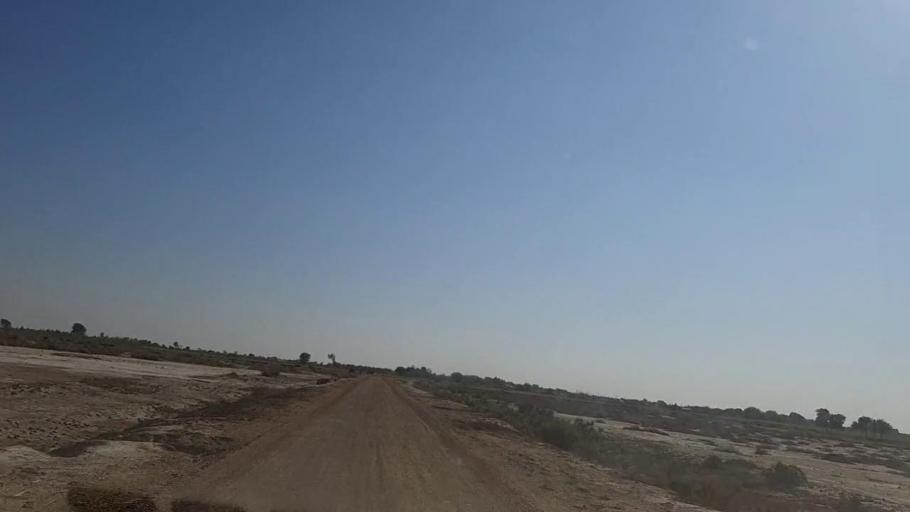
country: PK
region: Sindh
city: Digri
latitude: 25.1198
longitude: 69.0488
